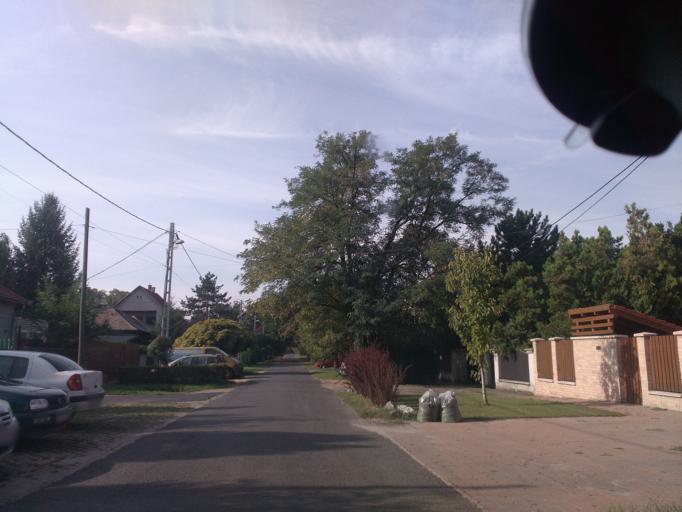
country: HU
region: Pest
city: Gyal
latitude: 47.4253
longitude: 19.2164
